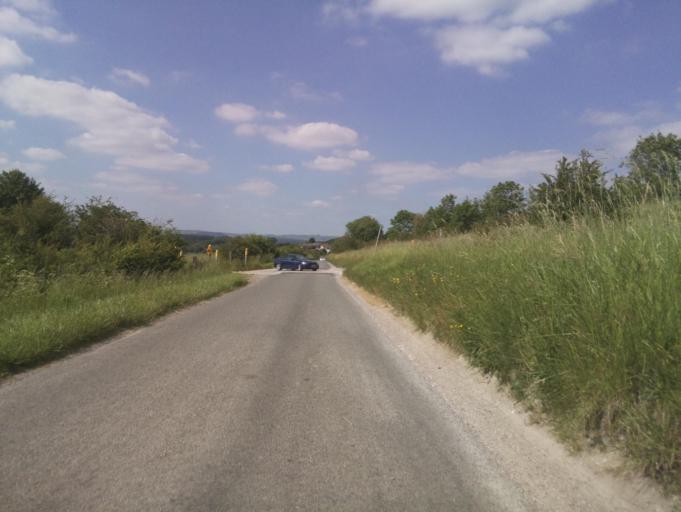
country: GB
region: England
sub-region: Wiltshire
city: Rushall
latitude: 51.2834
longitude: -1.8021
